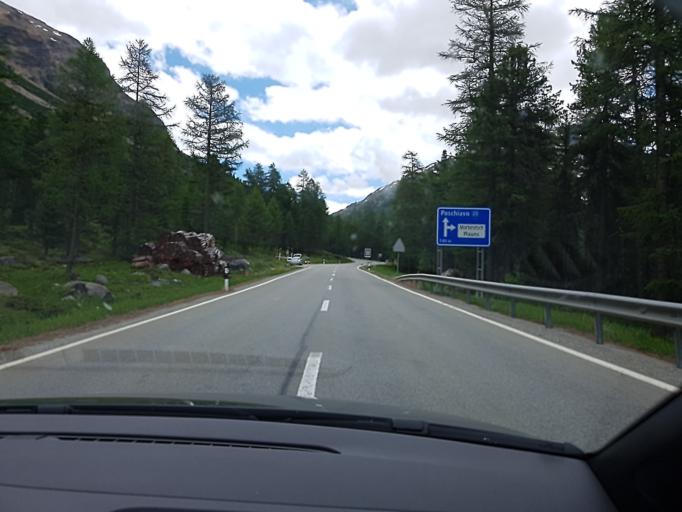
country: CH
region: Grisons
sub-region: Maloja District
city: Pontresina
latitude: 46.4643
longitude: 9.9337
